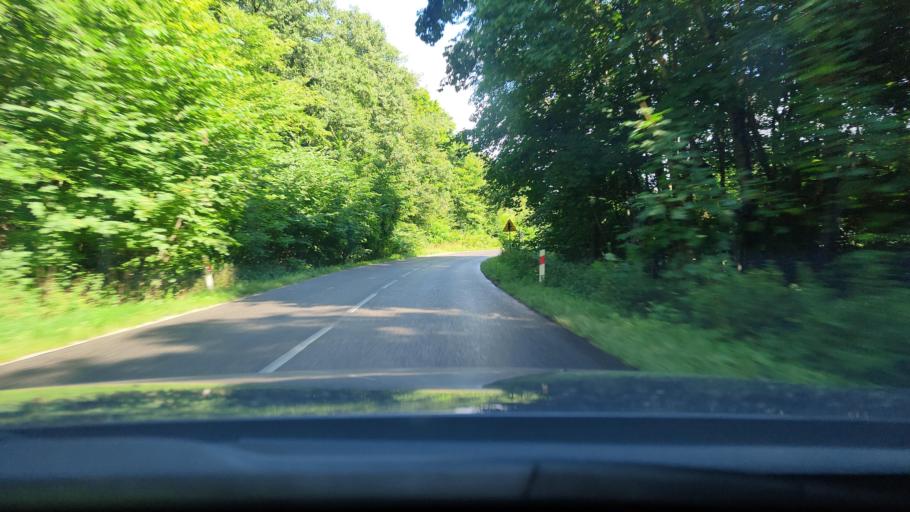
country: PL
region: Pomeranian Voivodeship
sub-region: Powiat pucki
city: Krokowa
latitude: 54.7504
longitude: 18.1736
